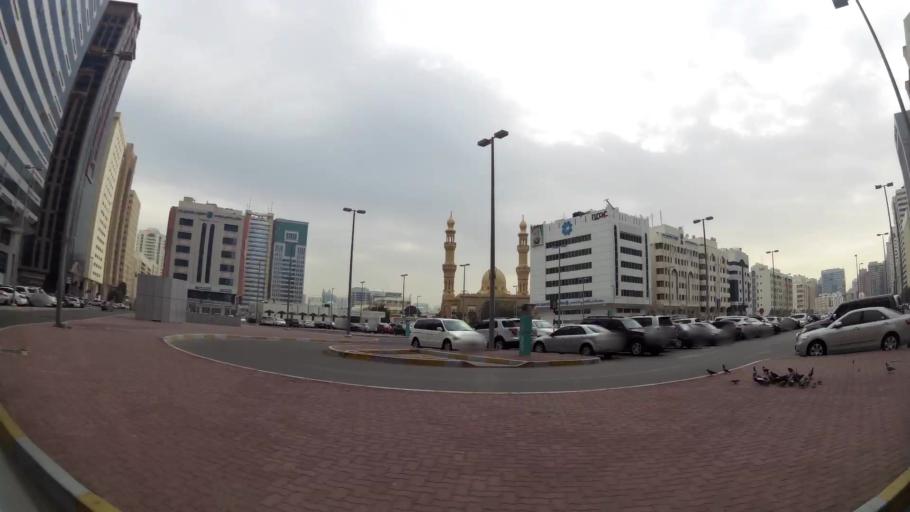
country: AE
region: Abu Dhabi
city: Abu Dhabi
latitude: 24.4828
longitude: 54.3604
